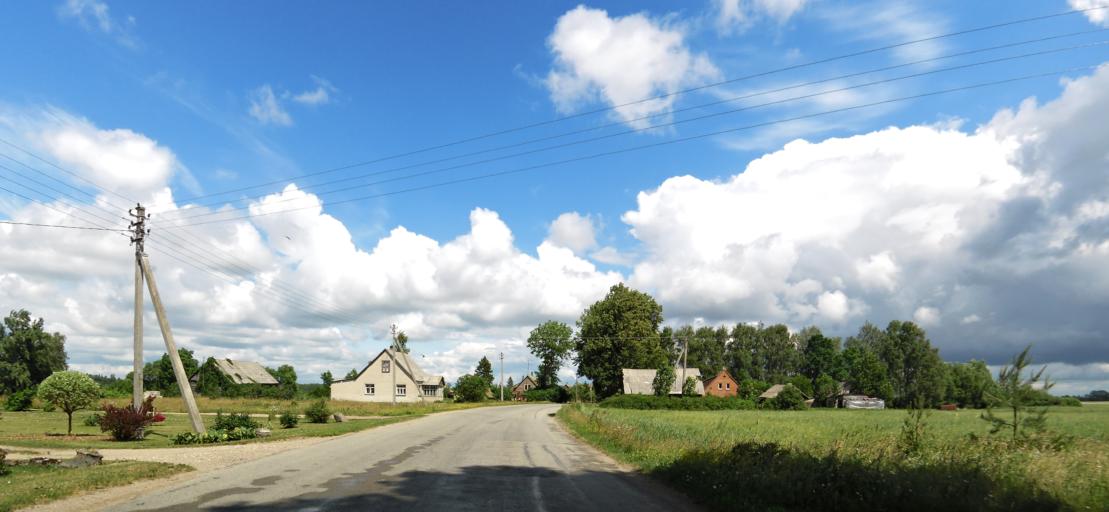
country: LT
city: Vabalninkas
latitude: 55.8863
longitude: 24.7866
